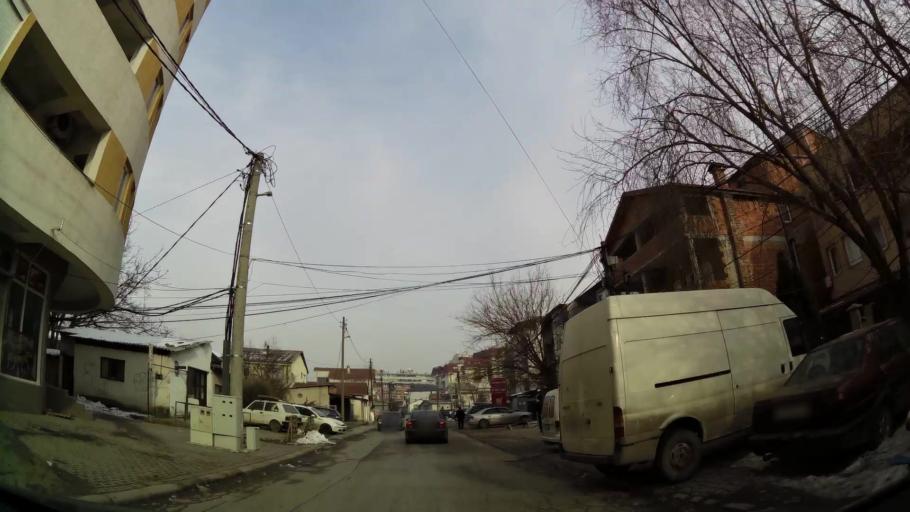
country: MK
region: Cair
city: Cair
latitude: 42.0115
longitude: 21.4416
